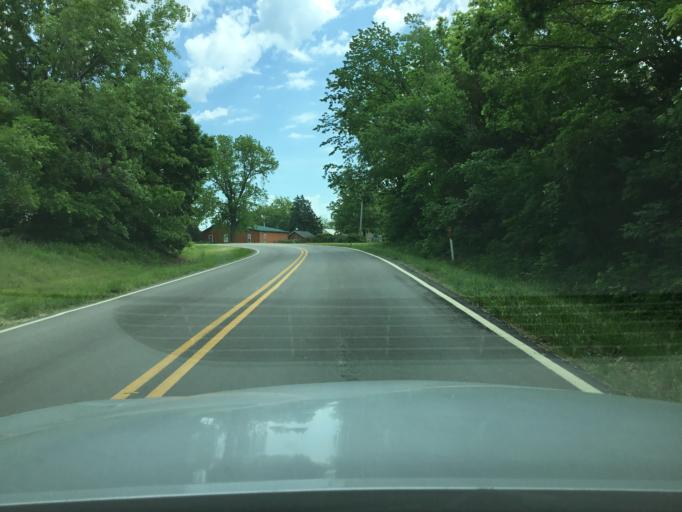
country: US
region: Kansas
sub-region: Montgomery County
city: Coffeyville
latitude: 37.0059
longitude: -95.5913
